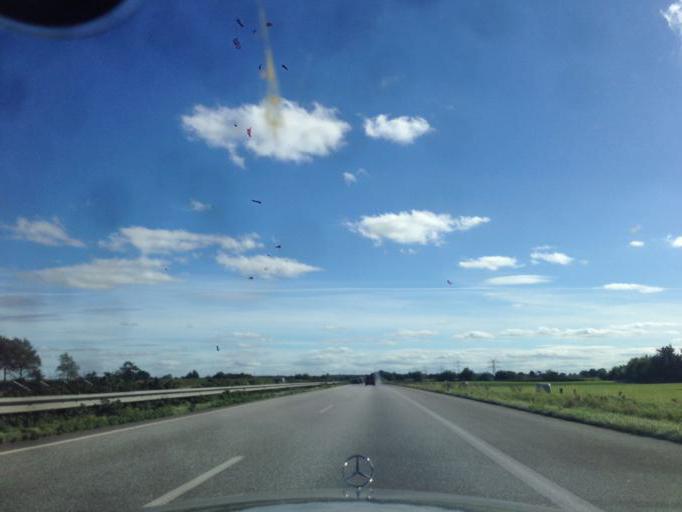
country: DE
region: Schleswig-Holstein
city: Sankelmark
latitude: 54.6971
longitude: 9.4056
